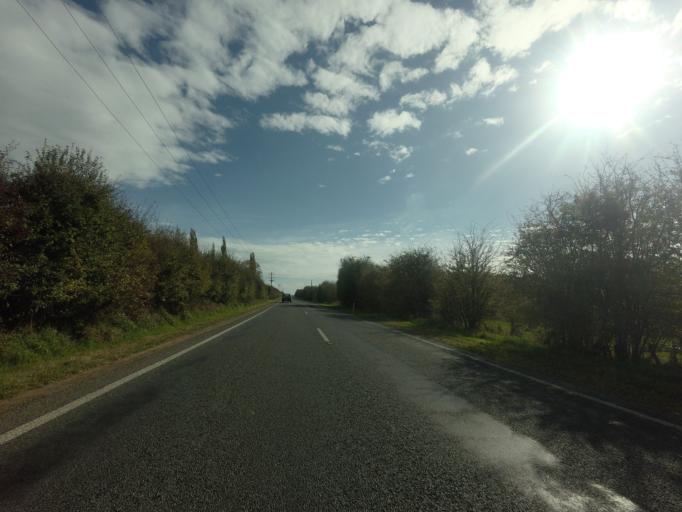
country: AU
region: Tasmania
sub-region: Meander Valley
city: Westbury
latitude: -41.5241
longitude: 146.7834
